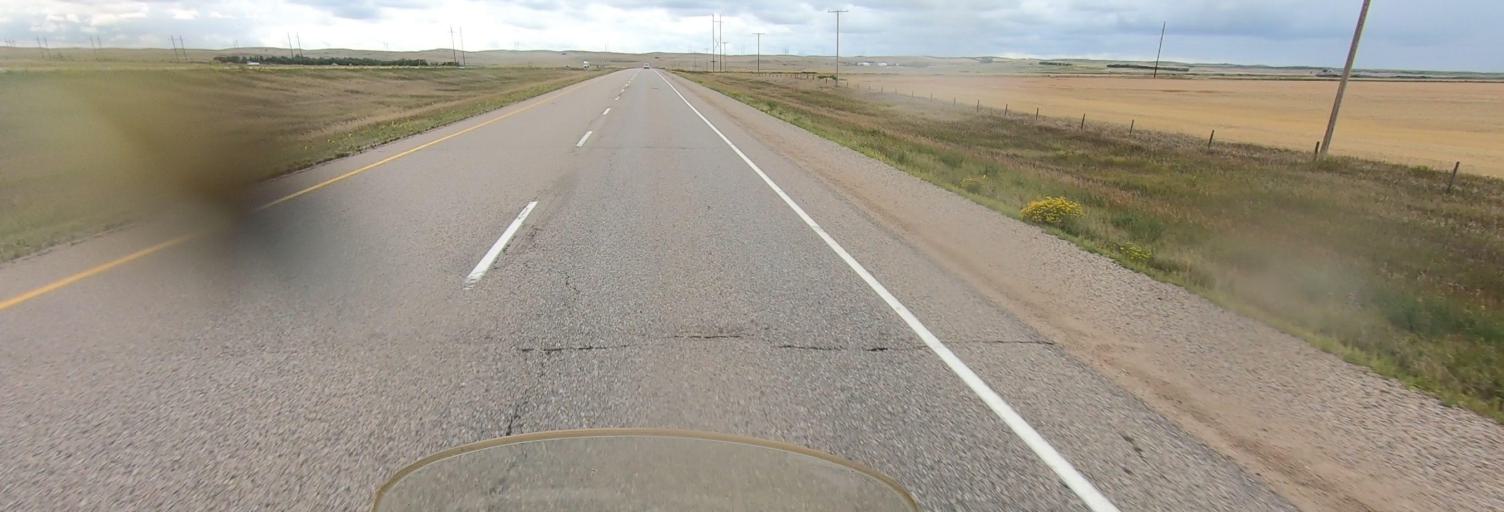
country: CA
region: Saskatchewan
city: Swift Current
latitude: 50.3979
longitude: -107.2827
